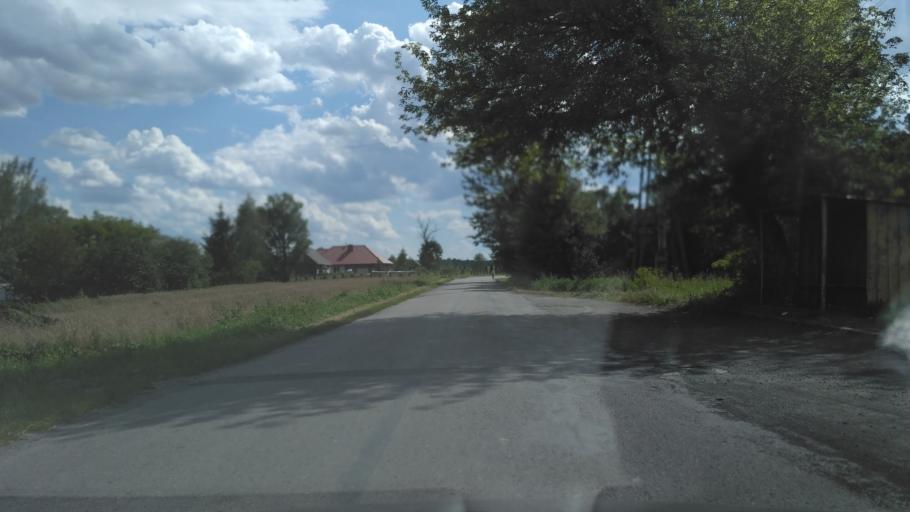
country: PL
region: Lublin Voivodeship
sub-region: Powiat leczynski
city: Milejow
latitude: 51.2130
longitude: 22.8868
